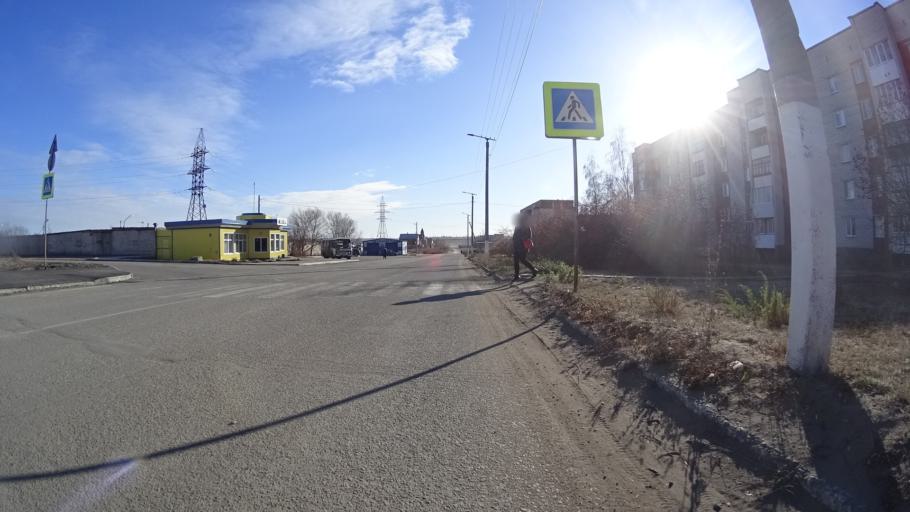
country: RU
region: Chelyabinsk
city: Troitsk
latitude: 54.0744
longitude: 61.5333
